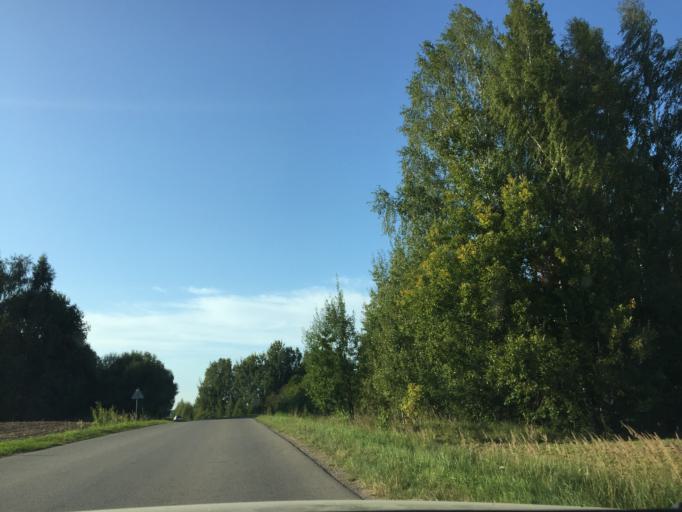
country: LT
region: Panevezys
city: Rokiskis
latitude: 55.8844
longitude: 25.6893
